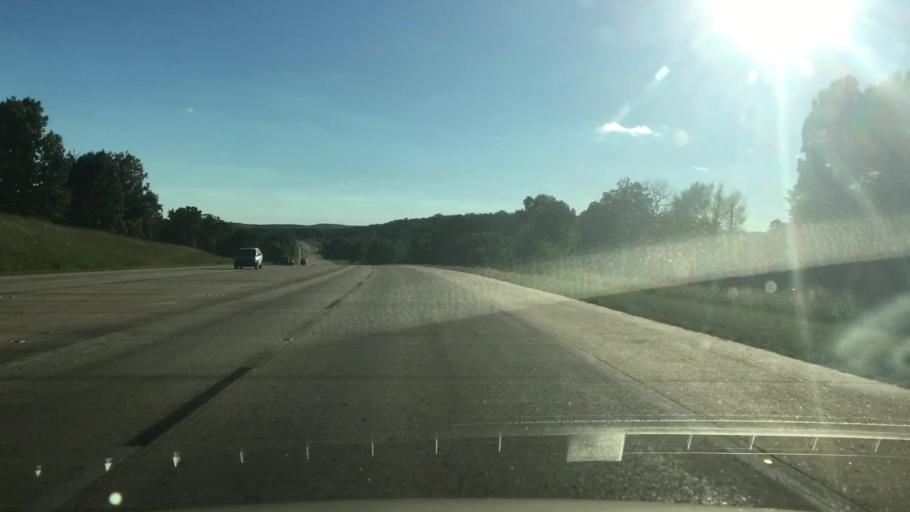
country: US
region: Oklahoma
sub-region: Cherokee County
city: Park Hill
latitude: 35.8453
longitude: -95.0285
